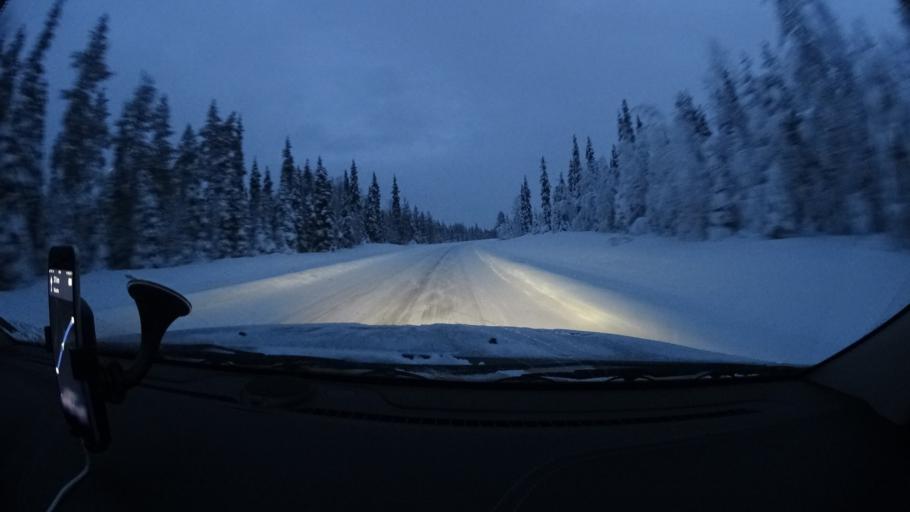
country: FI
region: Lapland
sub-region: Tunturi-Lappi
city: Kolari
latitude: 67.5351
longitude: 24.3262
